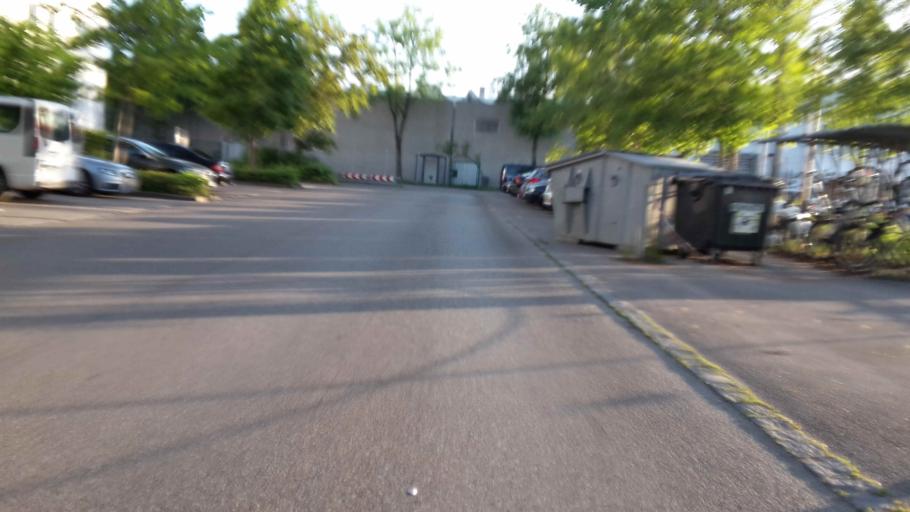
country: DE
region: Bavaria
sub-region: Upper Bavaria
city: Karlsfeld
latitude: 48.2187
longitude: 11.4811
